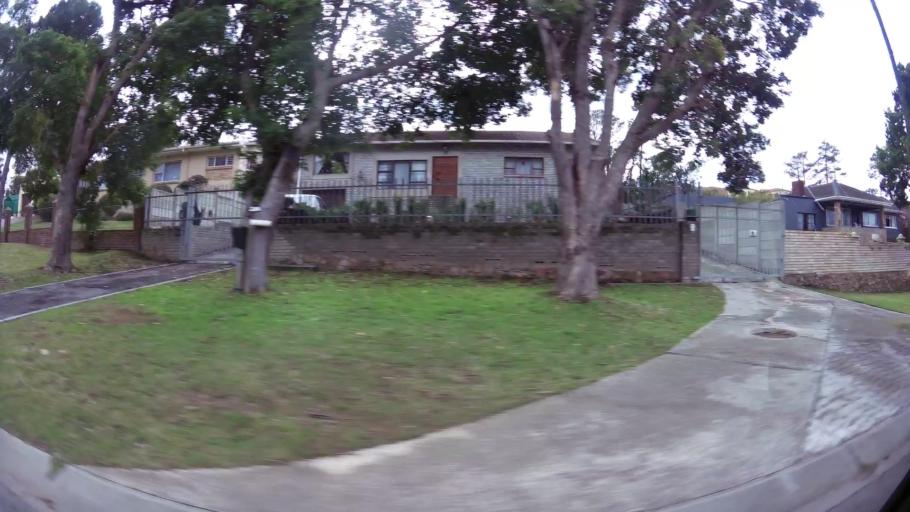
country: ZA
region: Eastern Cape
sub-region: Nelson Mandela Bay Metropolitan Municipality
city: Port Elizabeth
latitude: -33.9360
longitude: 25.5185
